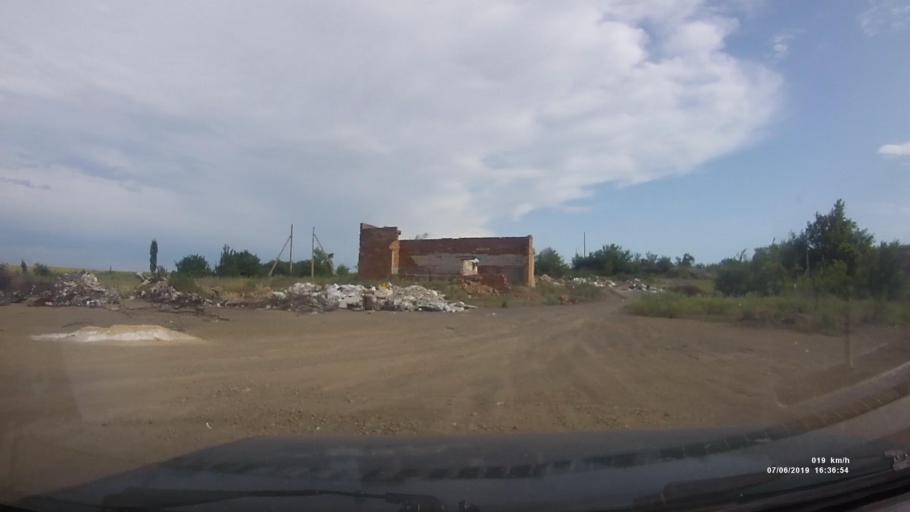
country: RU
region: Rostov
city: Staraya Stanitsa
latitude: 48.2520
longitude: 40.3520
